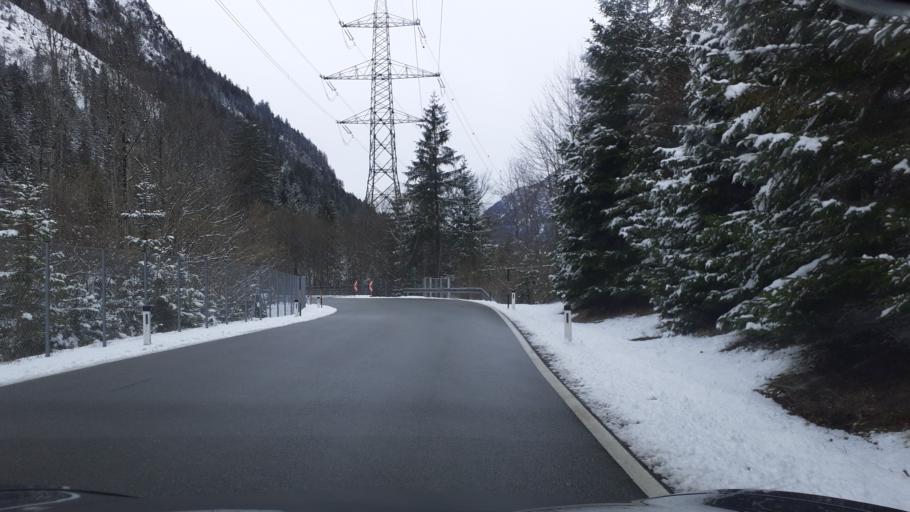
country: AT
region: Vorarlberg
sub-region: Politischer Bezirk Bludenz
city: Dalaas
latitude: 47.1293
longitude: 9.9615
